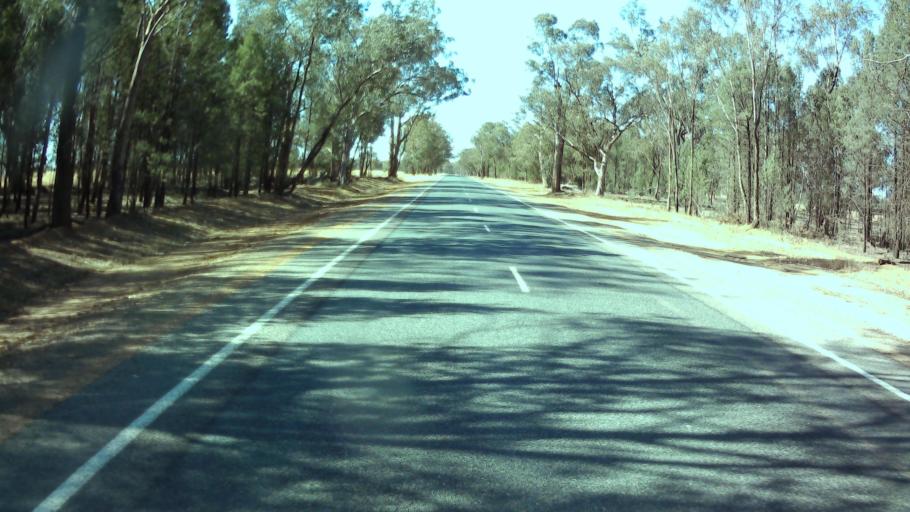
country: AU
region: New South Wales
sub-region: Weddin
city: Grenfell
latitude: -33.7413
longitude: 148.0887
